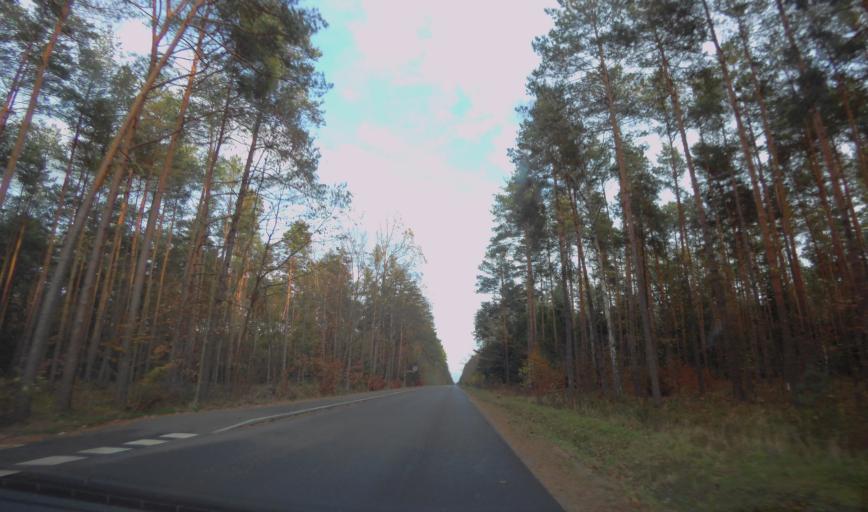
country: PL
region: Subcarpathian Voivodeship
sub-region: Powiat lezajski
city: Wola Zarczycka
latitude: 50.3282
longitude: 22.2847
